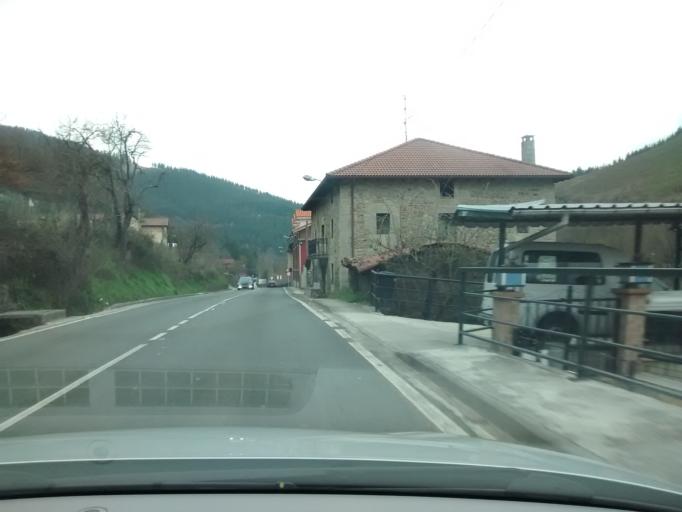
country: ES
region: Basque Country
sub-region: Bizkaia
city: Balmaseda
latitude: 43.1700
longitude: -3.2260
